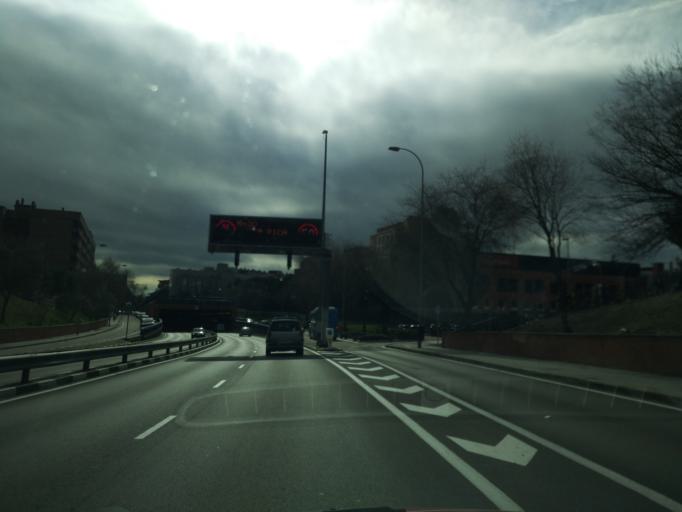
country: ES
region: Madrid
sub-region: Provincia de Madrid
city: Ciudad Lineal
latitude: 40.4662
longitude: -3.6570
